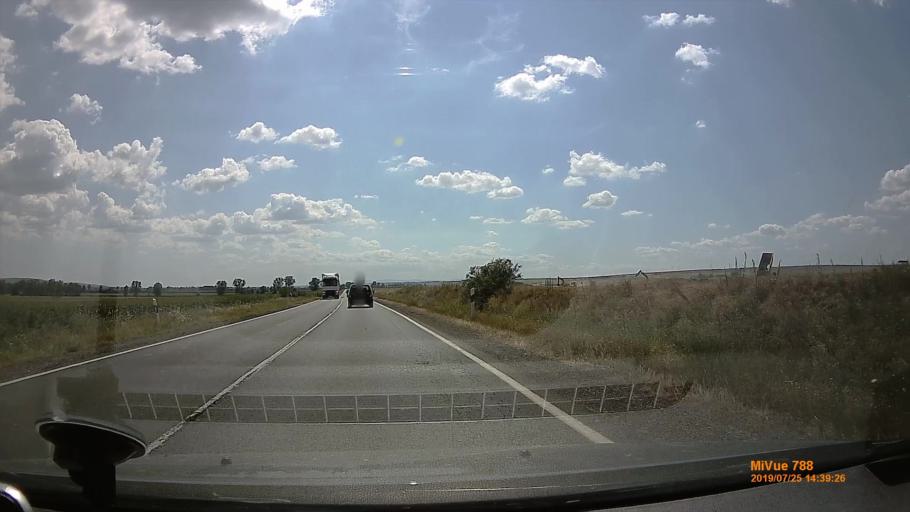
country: HU
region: Borsod-Abauj-Zemplen
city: Halmaj
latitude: 48.2994
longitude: 21.0533
